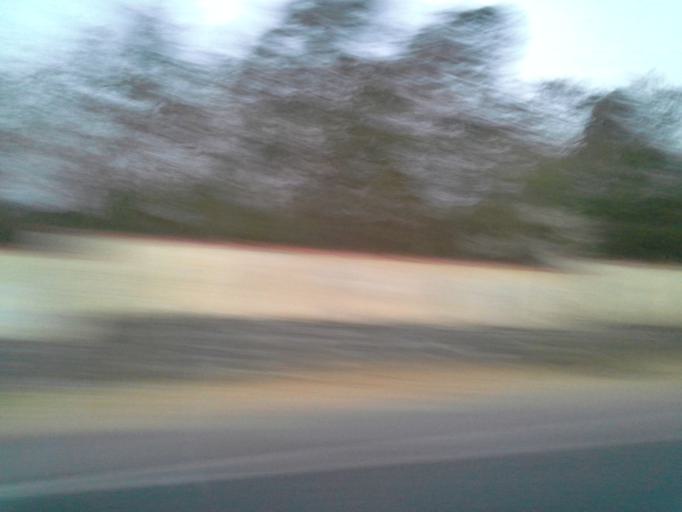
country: IN
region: Telangana
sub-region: Hyderabad
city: Hyderabad
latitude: 17.3228
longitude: 78.3824
